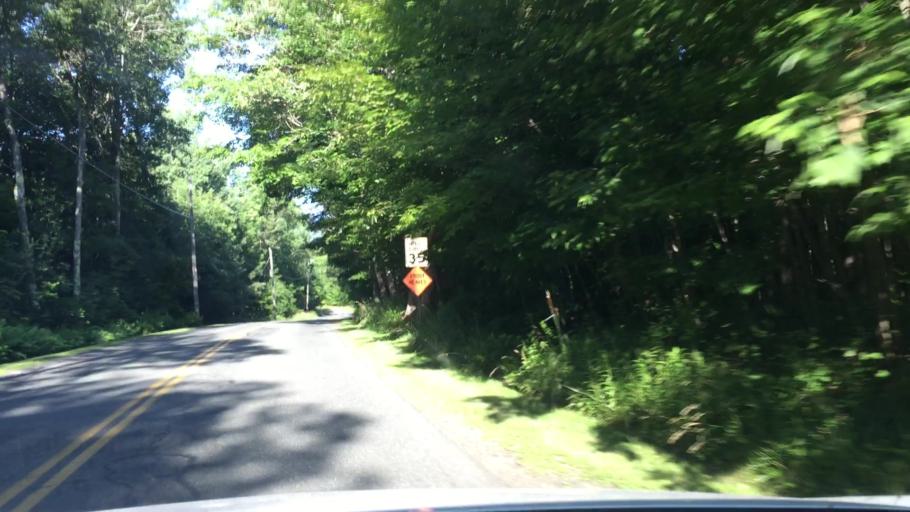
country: US
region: Massachusetts
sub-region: Berkshire County
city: Becket
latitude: 42.3173
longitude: -73.1118
